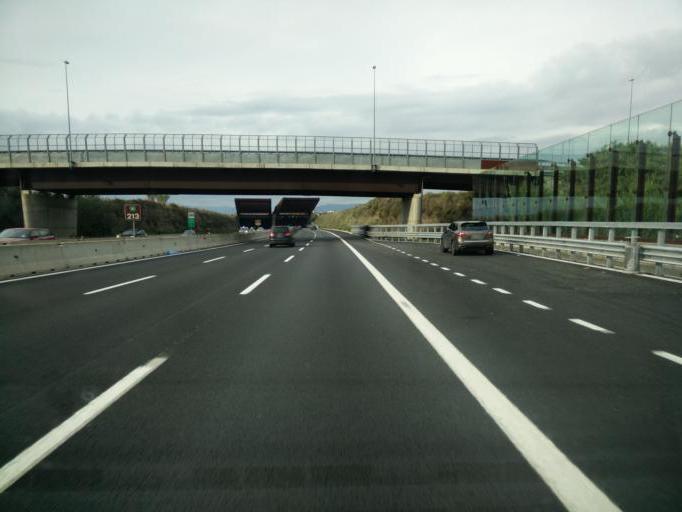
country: IT
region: Tuscany
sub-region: Province of Florence
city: Scandicci
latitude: 43.7601
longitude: 11.1701
